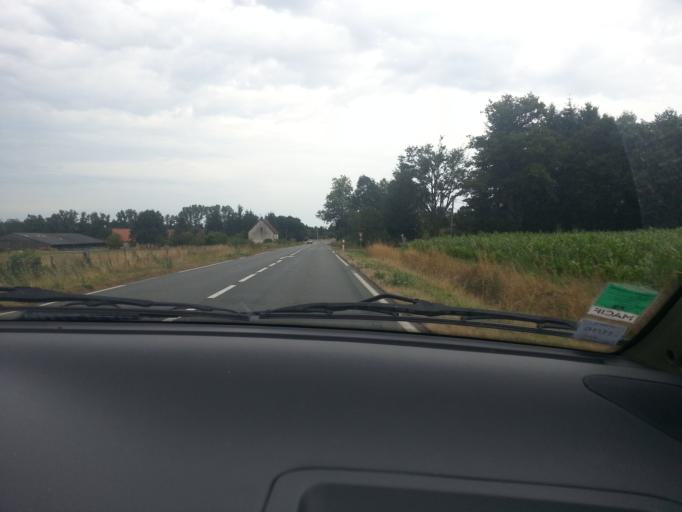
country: FR
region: Auvergne
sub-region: Departement de l'Allier
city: Saint-Gerand-le-Puy
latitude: 46.2035
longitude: 3.4989
